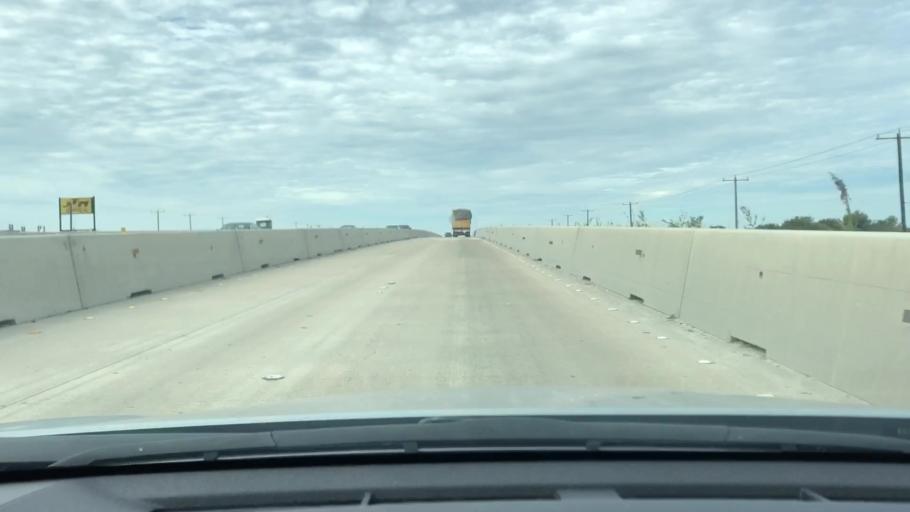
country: US
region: Texas
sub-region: Bexar County
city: Kirby
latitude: 29.4507
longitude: -98.3441
